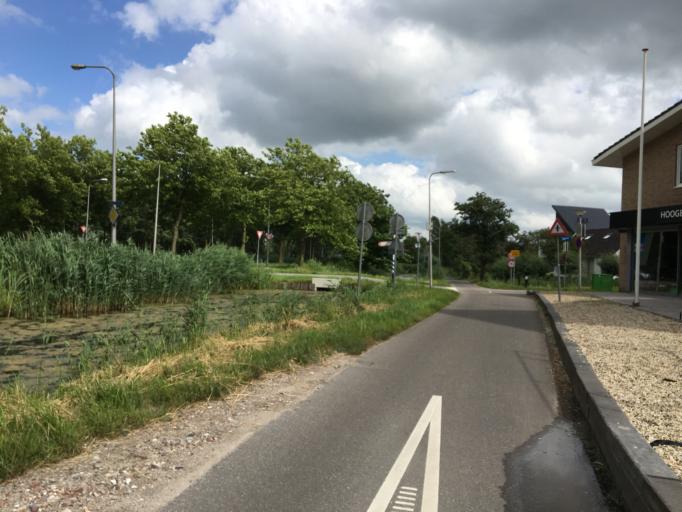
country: NL
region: South Holland
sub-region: Gemeente Gouda
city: Gouda
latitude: 52.0176
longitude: 4.7329
